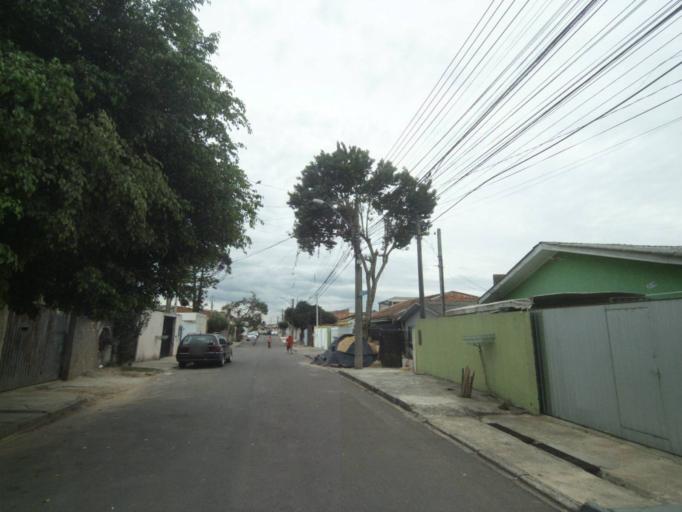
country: BR
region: Parana
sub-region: Curitiba
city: Curitiba
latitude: -25.5052
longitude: -49.3374
